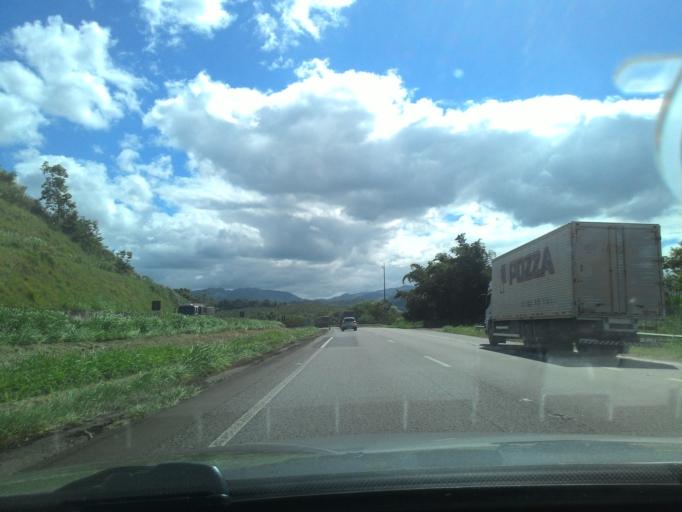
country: BR
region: Sao Paulo
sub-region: Cajati
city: Cajati
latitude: -24.7535
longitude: -48.1592
